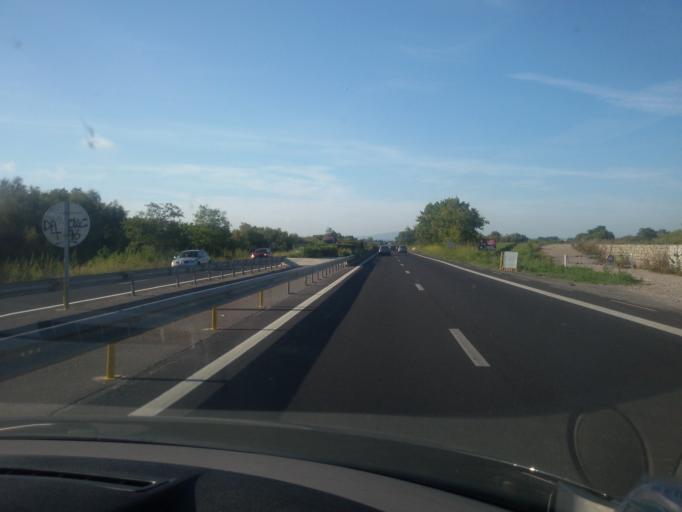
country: FR
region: Languedoc-Roussillon
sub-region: Departement de l'Herault
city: Lattes
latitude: 43.5427
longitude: 3.8967
